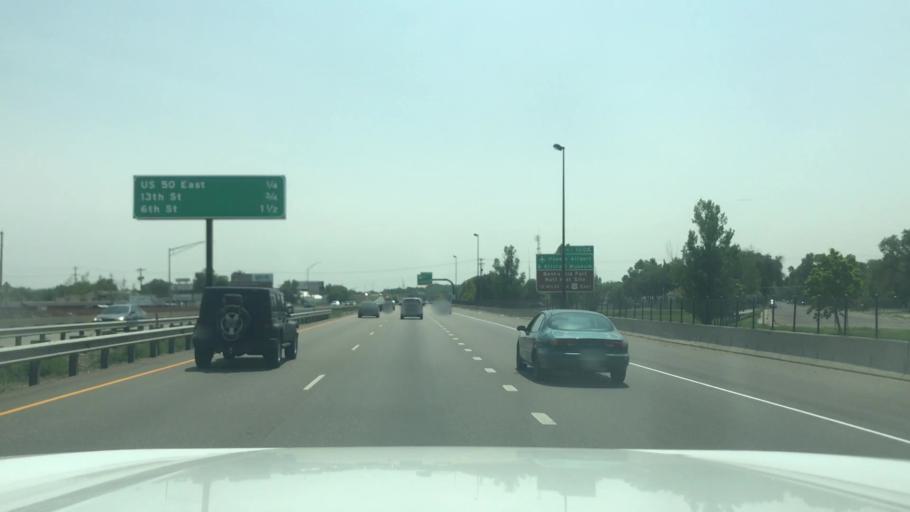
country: US
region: Colorado
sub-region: Pueblo County
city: Pueblo
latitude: 38.2933
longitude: -104.6089
